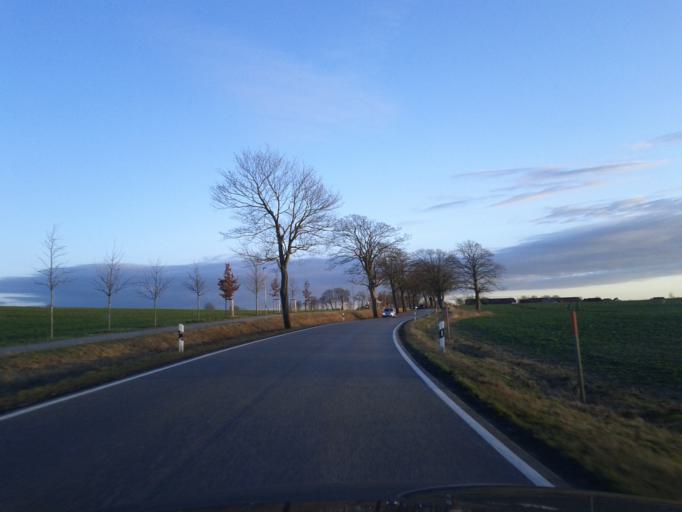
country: DE
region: Mecklenburg-Vorpommern
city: Hornstorf
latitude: 53.9420
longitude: 11.4865
